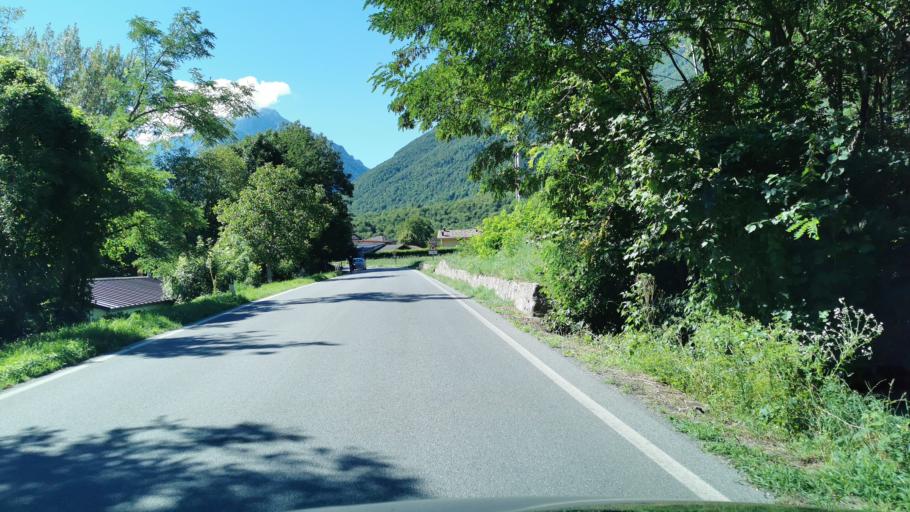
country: IT
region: Piedmont
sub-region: Provincia di Cuneo
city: Valdieri
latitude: 44.2613
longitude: 7.3817
